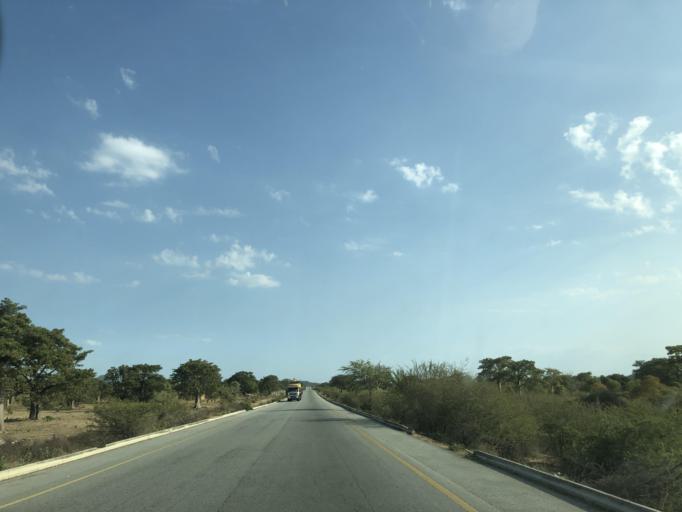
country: AO
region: Benguela
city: Benguela
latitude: -13.2104
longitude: 13.7643
